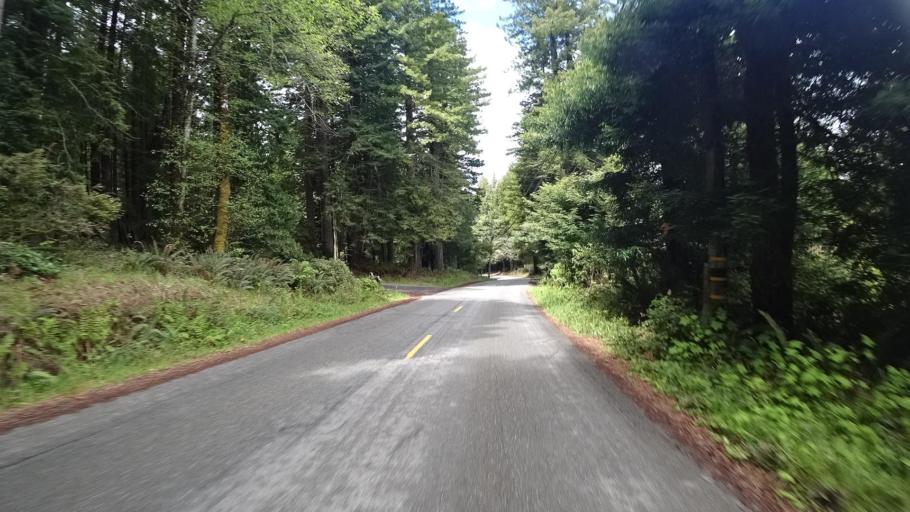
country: US
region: California
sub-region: Humboldt County
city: Bayside
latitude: 40.8003
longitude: -124.0391
